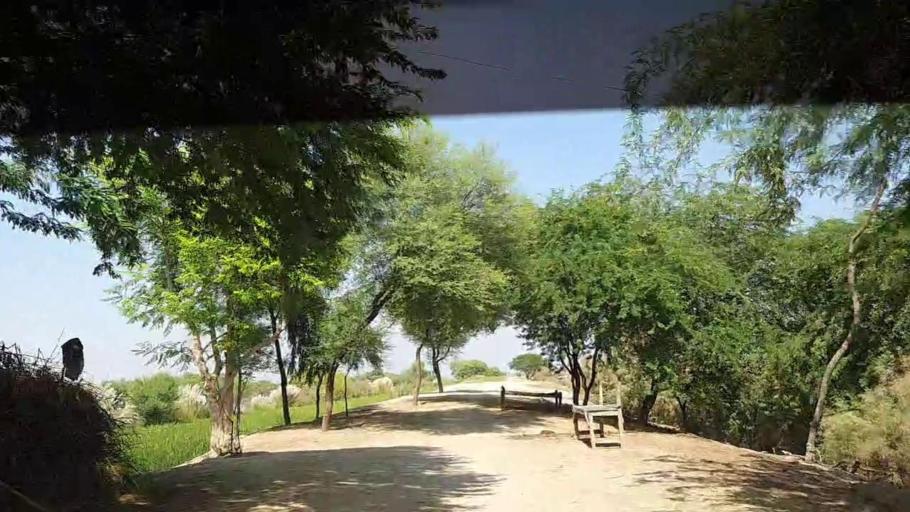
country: PK
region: Sindh
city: Kandhkot
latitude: 28.1795
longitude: 69.1521
